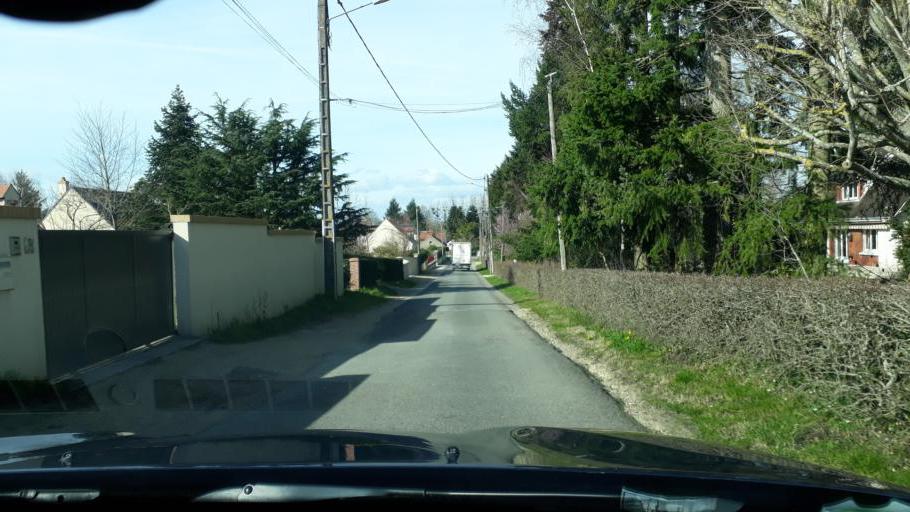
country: FR
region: Centre
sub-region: Departement du Loiret
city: Donnery
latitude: 47.9123
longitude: 2.1095
